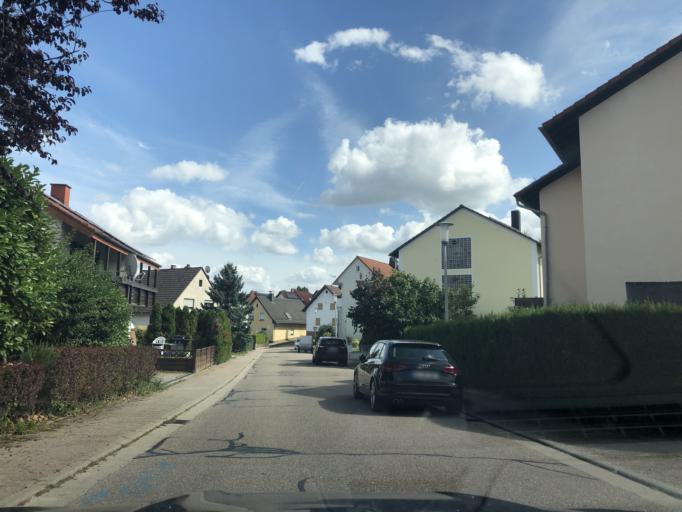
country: DE
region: Baden-Wuerttemberg
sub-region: Karlsruhe Region
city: Gaiberg
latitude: 49.3409
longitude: 8.7511
